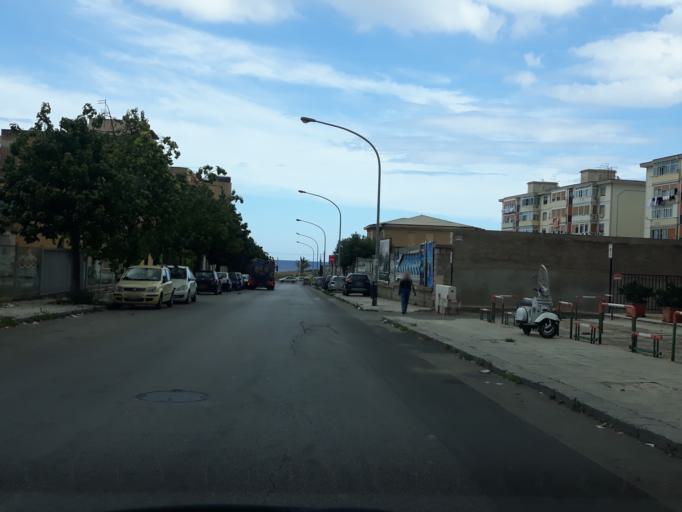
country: IT
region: Sicily
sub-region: Palermo
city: Ciaculli
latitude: 38.1014
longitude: 13.3938
